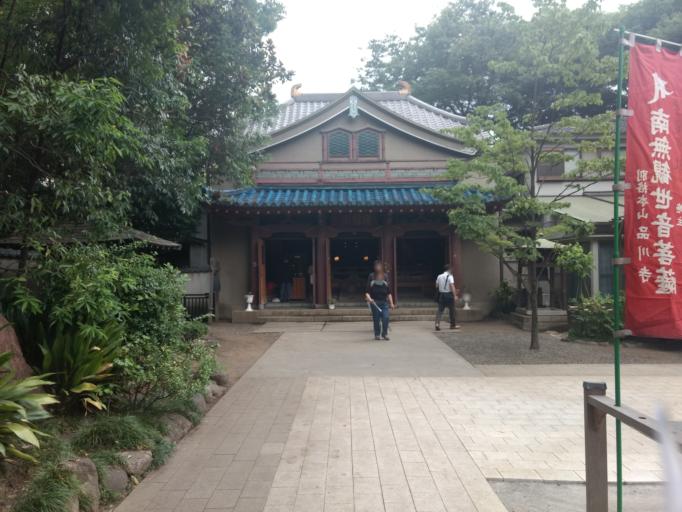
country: JP
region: Kanagawa
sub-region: Kawasaki-shi
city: Kawasaki
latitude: 35.6095
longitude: 139.7437
